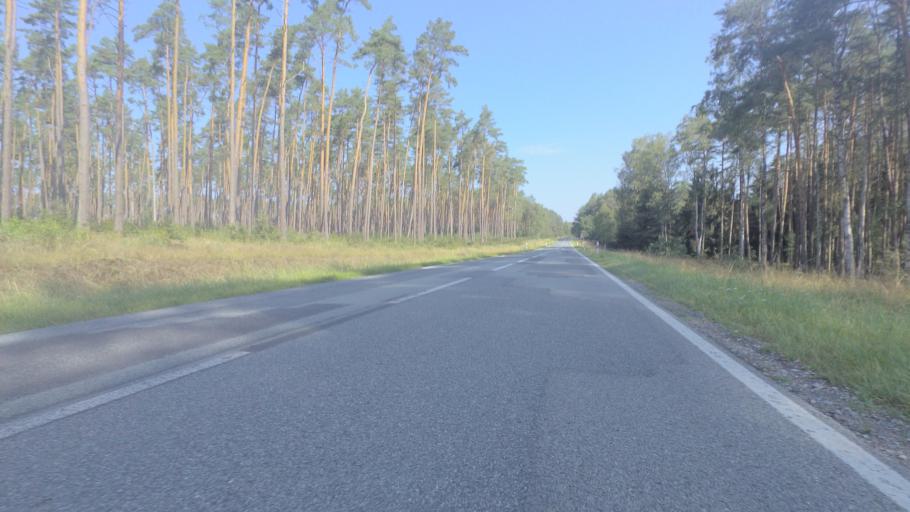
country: DE
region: Mecklenburg-Vorpommern
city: Malchow
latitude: 53.5621
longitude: 12.4532
